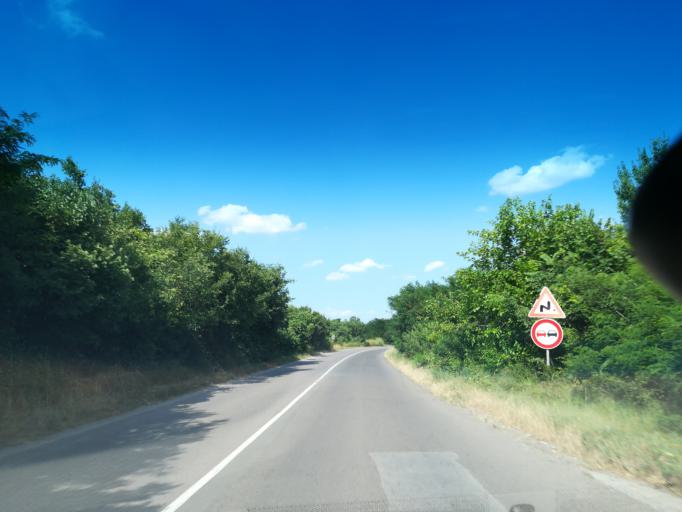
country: BG
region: Stara Zagora
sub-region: Obshtina Chirpan
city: Chirpan
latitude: 42.2078
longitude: 25.3586
